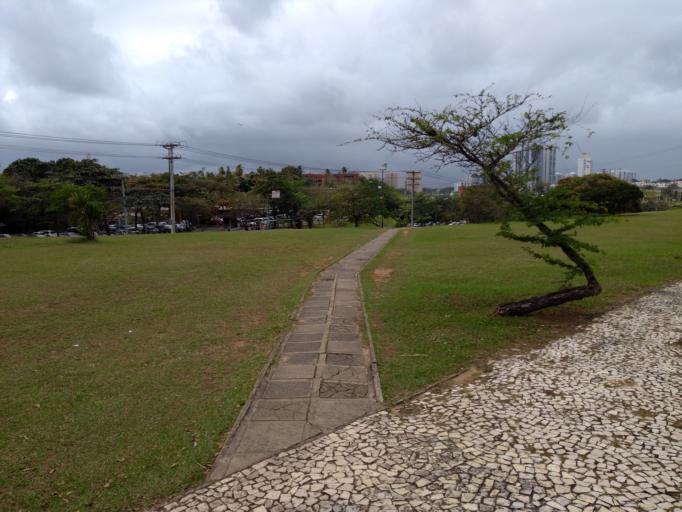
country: BR
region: Bahia
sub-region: Salvador
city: Salvador
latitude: -12.9441
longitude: -38.4234
